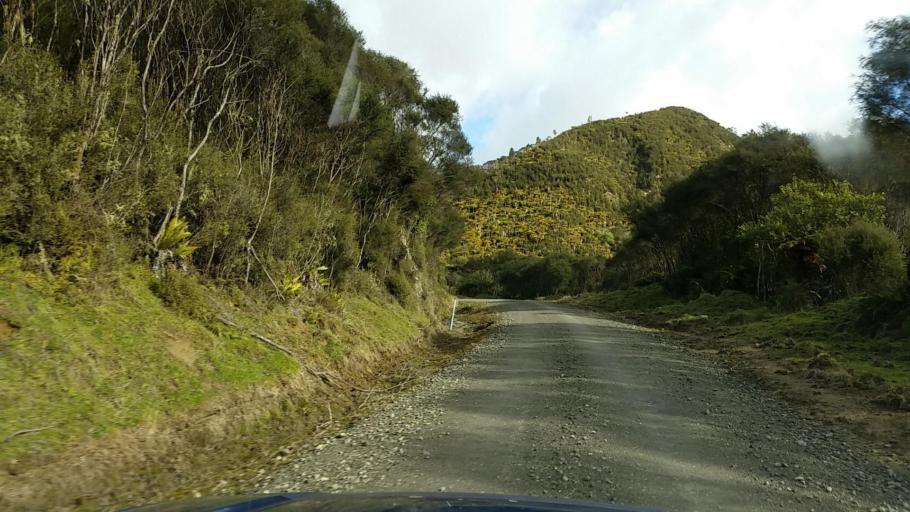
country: NZ
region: Taranaki
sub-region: South Taranaki District
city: Eltham
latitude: -39.2683
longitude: 174.7439
